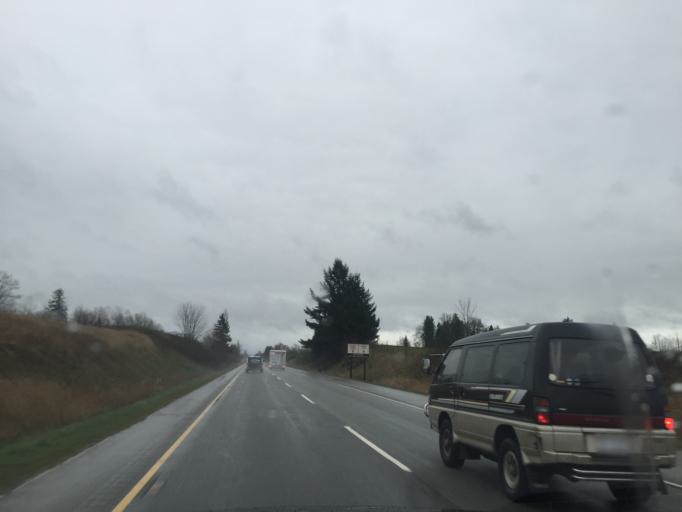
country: CA
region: British Columbia
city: Aldergrove
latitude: 49.0922
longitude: -122.4695
